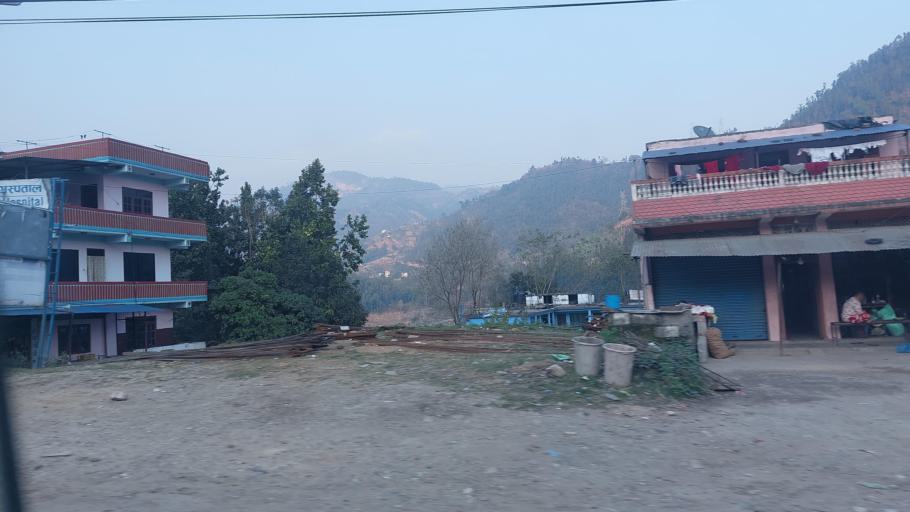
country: NP
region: Central Region
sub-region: Narayani Zone
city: Bharatpur
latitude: 27.8111
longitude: 84.8333
